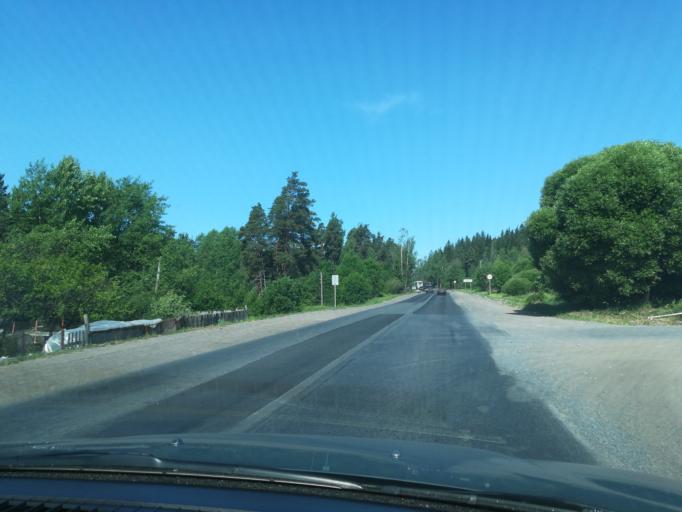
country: RU
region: Leningrad
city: Svetogorsk
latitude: 61.0898
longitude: 28.9002
